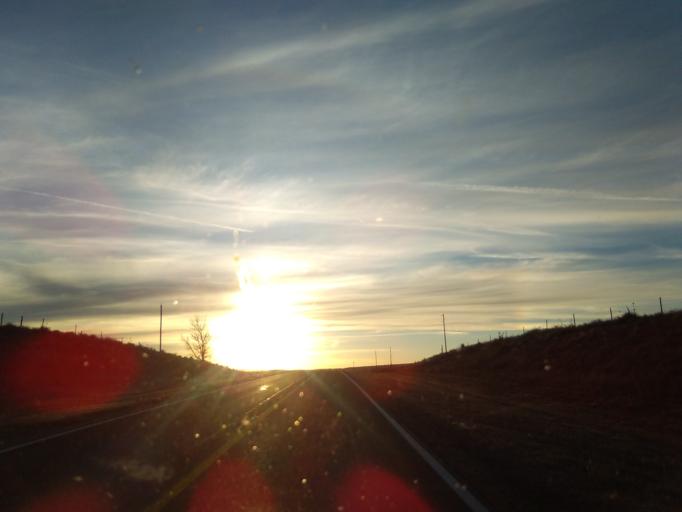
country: US
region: Kansas
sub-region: Wallace County
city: Sharon Springs
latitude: 39.0145
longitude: -101.3557
